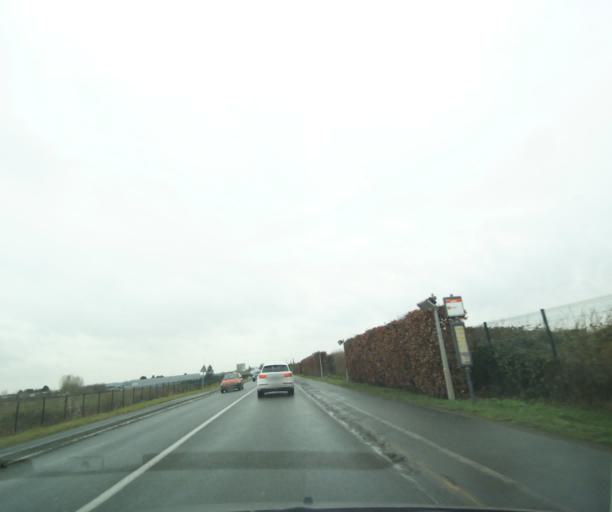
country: FR
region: Nord-Pas-de-Calais
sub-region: Departement du Nord
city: Prouvy
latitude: 50.3304
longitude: 3.4482
